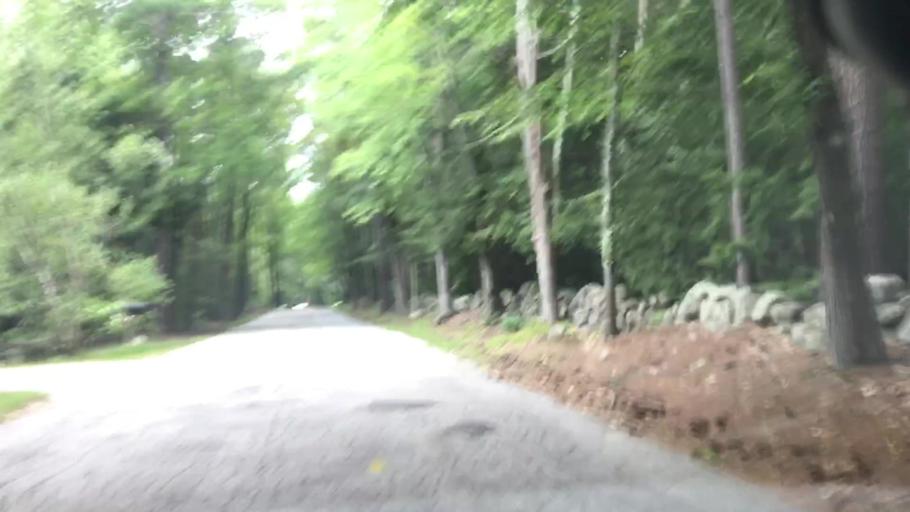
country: US
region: New Hampshire
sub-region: Hillsborough County
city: Milford
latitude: 42.8548
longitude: -71.6327
